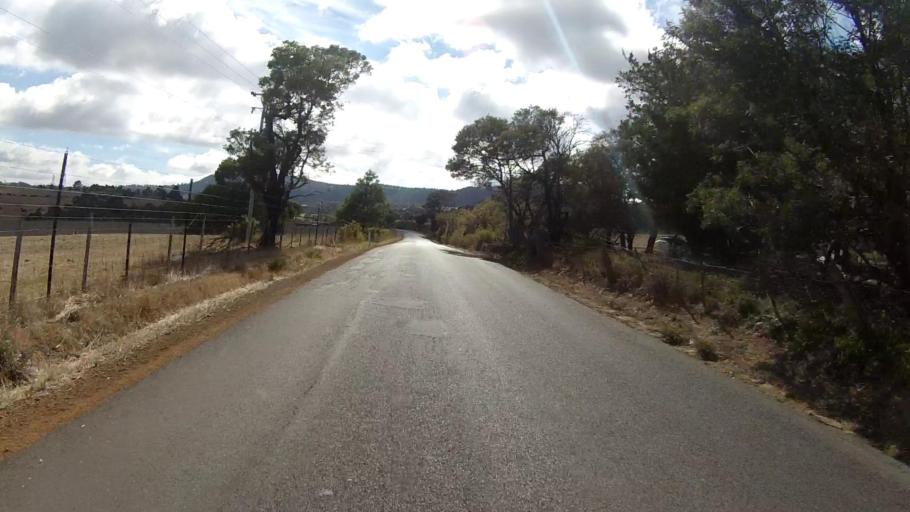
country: AU
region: Tasmania
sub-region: Brighton
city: Old Beach
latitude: -42.7717
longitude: 147.2904
